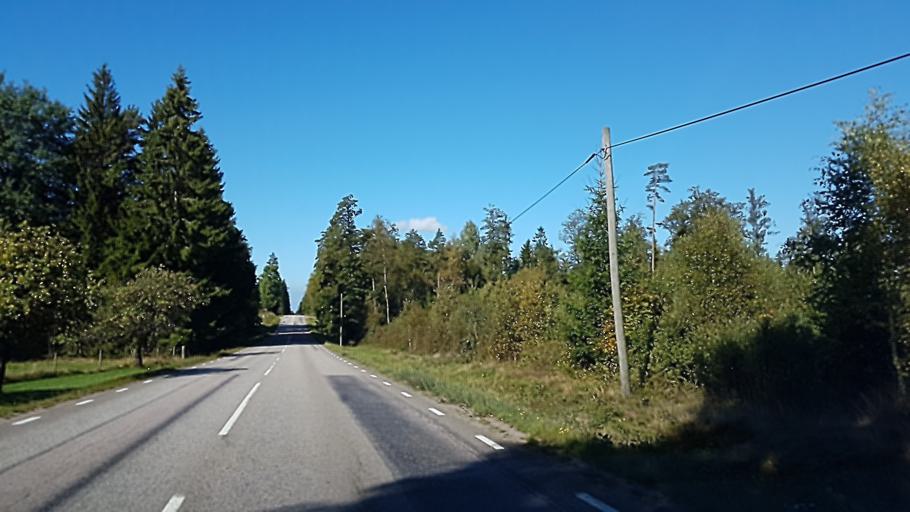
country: SE
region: Kronoberg
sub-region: Ljungby Kommun
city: Ljungby
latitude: 56.8264
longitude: 14.0252
